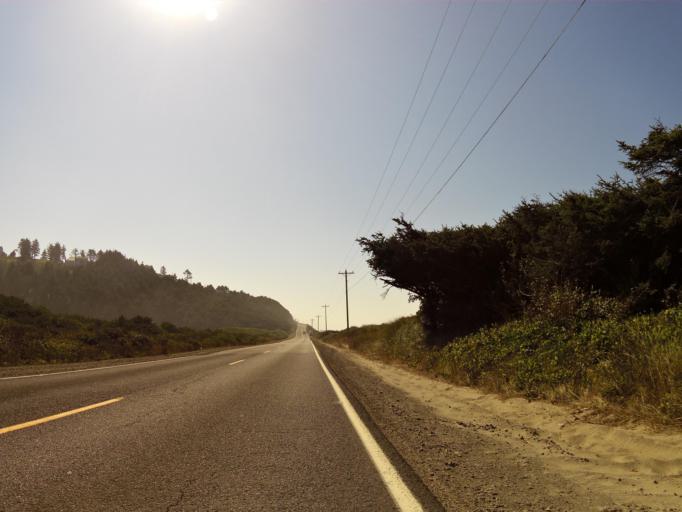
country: US
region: Oregon
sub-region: Tillamook County
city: Pacific City
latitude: 45.2446
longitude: -123.9679
